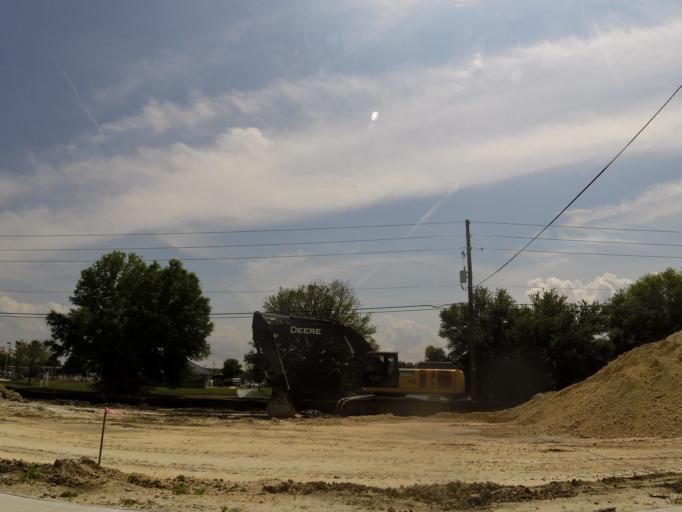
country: US
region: Florida
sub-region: Nassau County
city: Yulee
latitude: 30.5177
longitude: -81.6401
